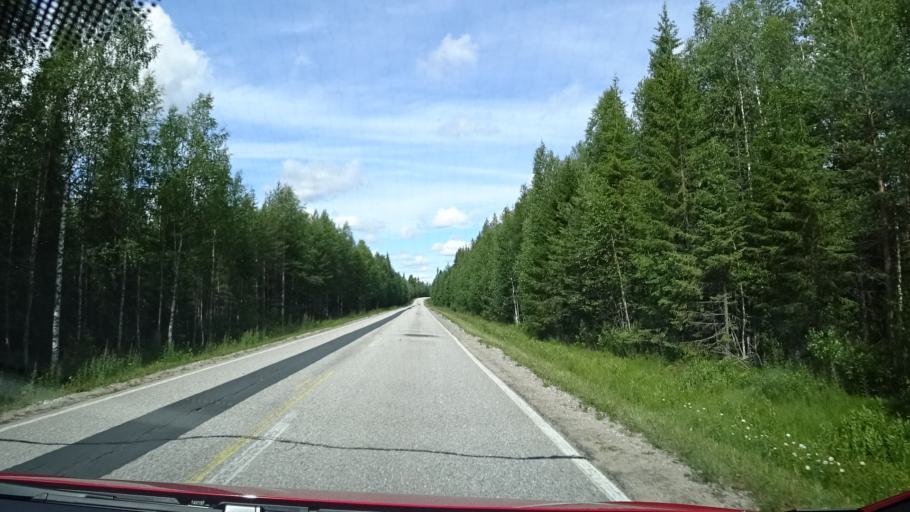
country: FI
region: Kainuu
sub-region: Kehys-Kainuu
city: Kuhmo
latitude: 64.4512
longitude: 29.7811
